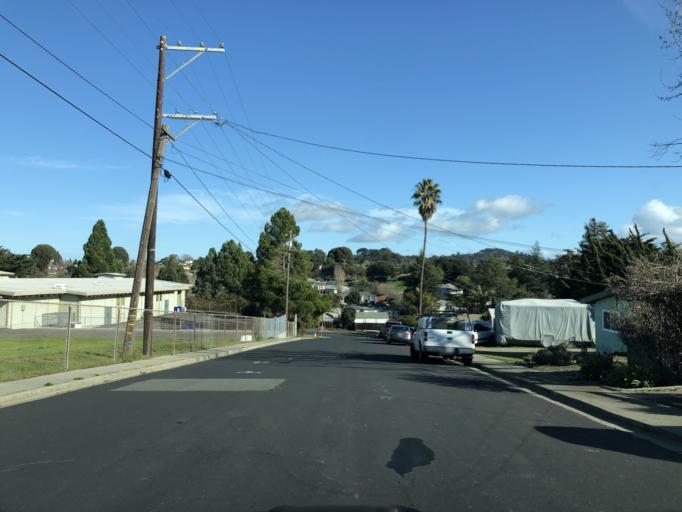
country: US
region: California
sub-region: Contra Costa County
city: Tara Hills
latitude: 37.9843
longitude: -122.3087
